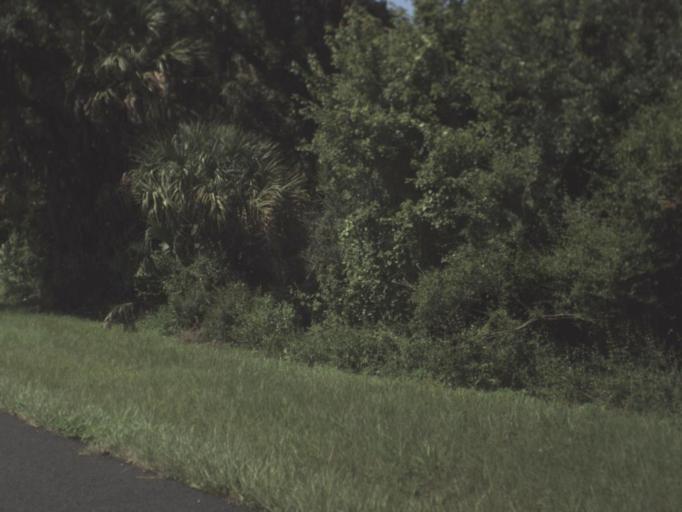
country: US
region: Florida
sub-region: Citrus County
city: Crystal River
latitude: 28.9494
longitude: -82.6251
